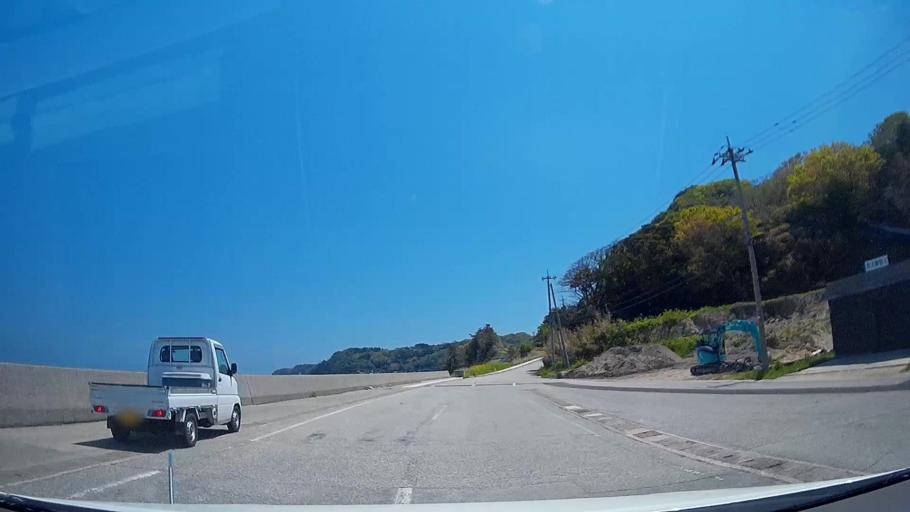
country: JP
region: Ishikawa
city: Nanao
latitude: 37.5295
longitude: 137.2900
